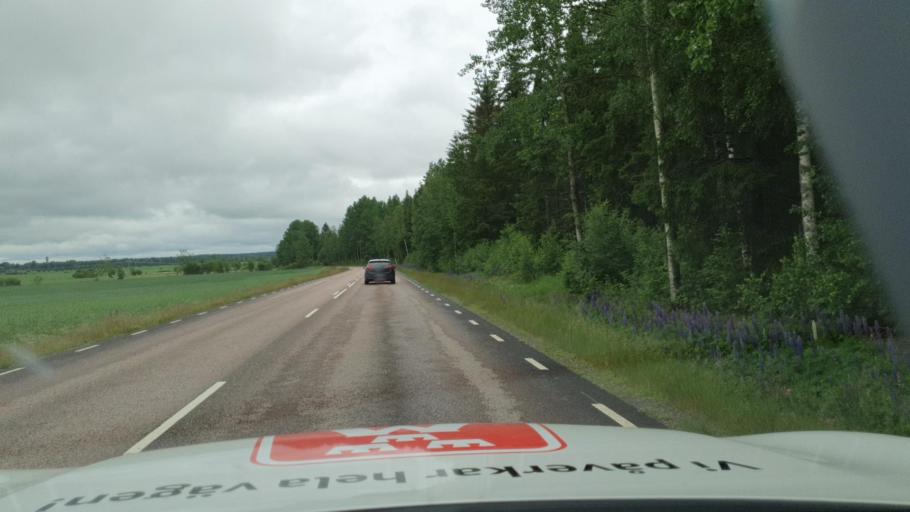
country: SE
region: Vaermland
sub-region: Karlstads Kommun
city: Edsvalla
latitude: 59.4134
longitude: 13.2149
